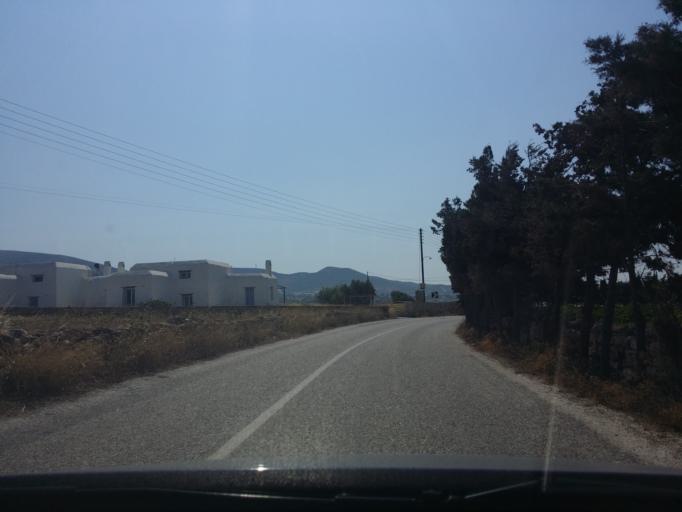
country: GR
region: South Aegean
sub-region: Nomos Kykladon
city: Antiparos
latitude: 37.0082
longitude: 25.1228
